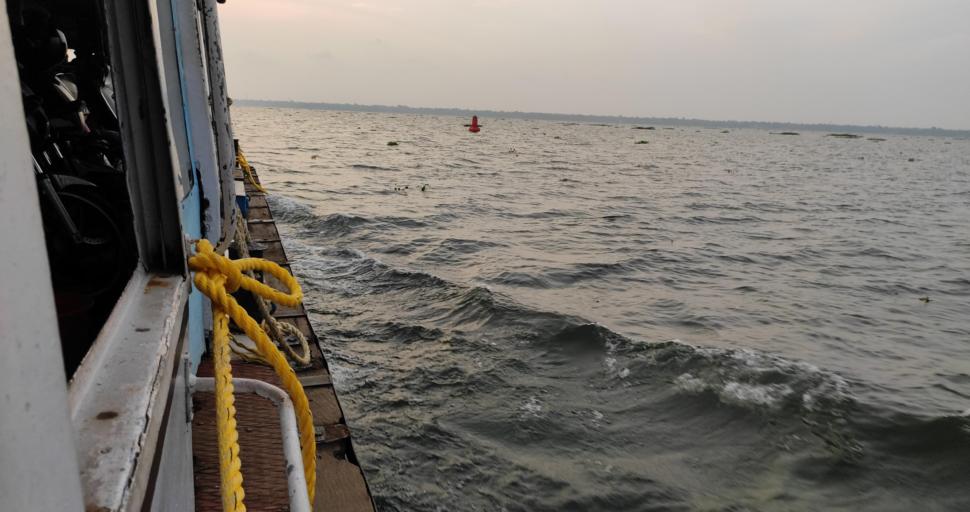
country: IN
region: Kerala
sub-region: Alappuzha
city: Shertallai
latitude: 9.6032
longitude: 76.3891
